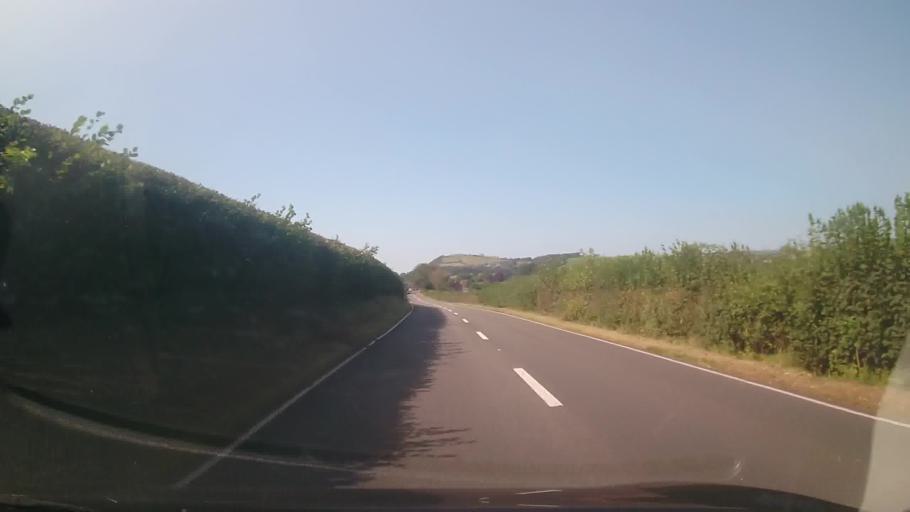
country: GB
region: Wales
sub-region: Carmarthenshire
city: Llanddarog
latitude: 51.8743
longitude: -4.1616
